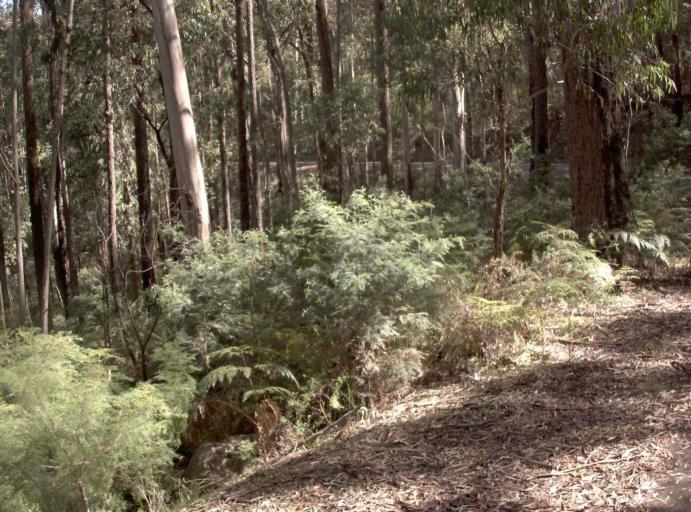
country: AU
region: Victoria
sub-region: East Gippsland
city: Lakes Entrance
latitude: -37.3938
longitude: 148.1233
